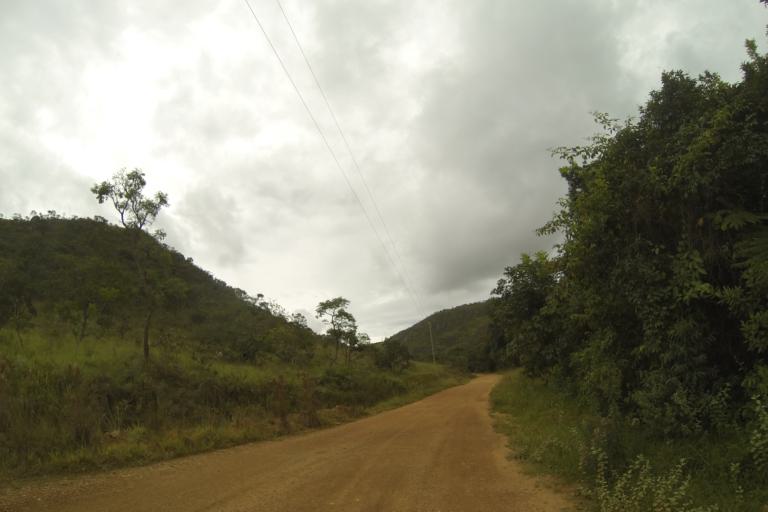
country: BR
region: Minas Gerais
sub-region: Ibia
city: Ibia
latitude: -19.7523
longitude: -46.5101
